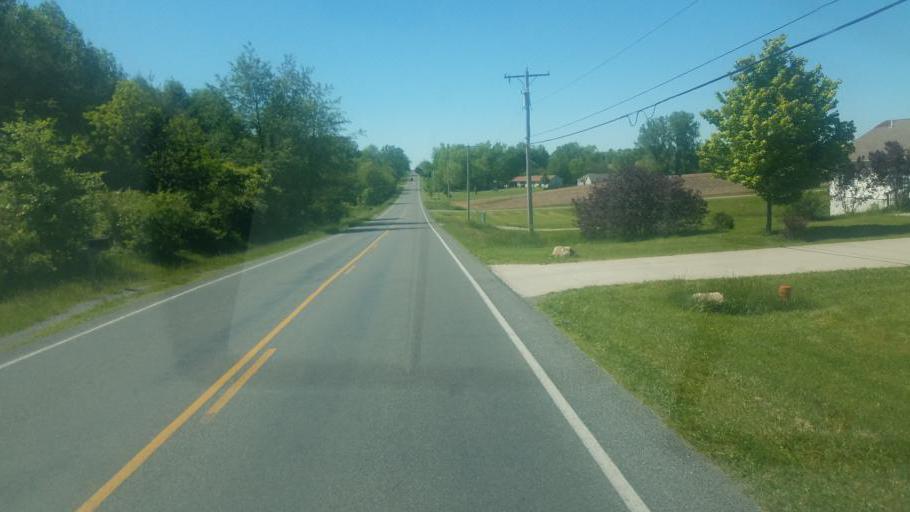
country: US
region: Ohio
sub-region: Logan County
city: Bellefontaine
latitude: 40.3822
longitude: -83.7826
